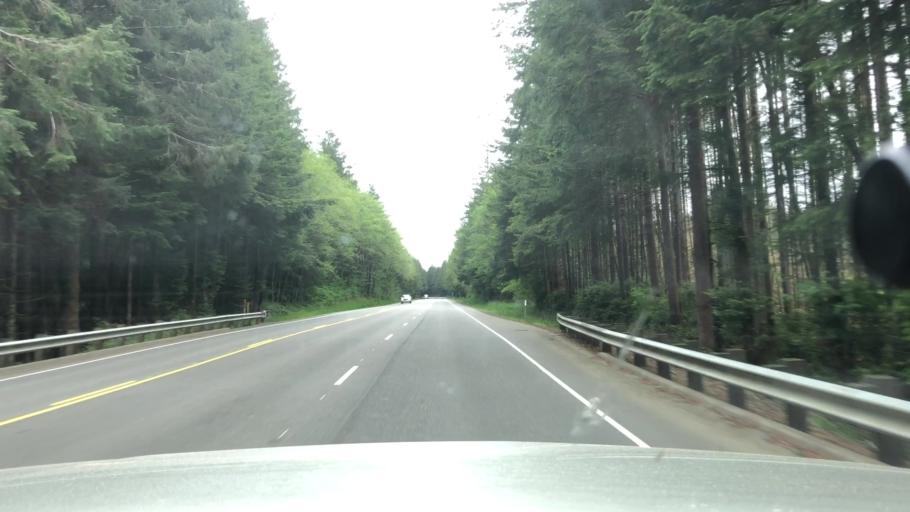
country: US
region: Oregon
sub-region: Coos County
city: Coquille
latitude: 43.2230
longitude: -124.3013
